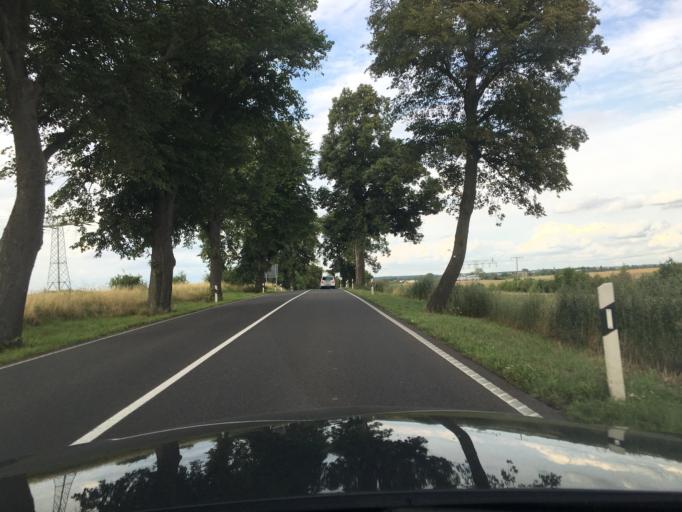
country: DE
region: Mecklenburg-Vorpommern
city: Gross Nemerow
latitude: 53.4625
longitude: 13.2000
